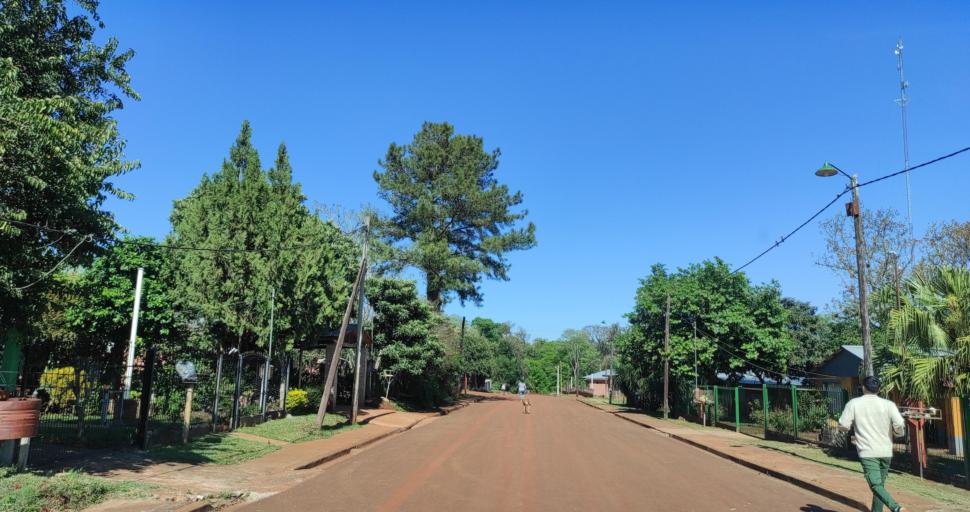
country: AR
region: Misiones
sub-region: Departamento de Candelaria
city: Loreto
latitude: -27.3319
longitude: -55.5240
